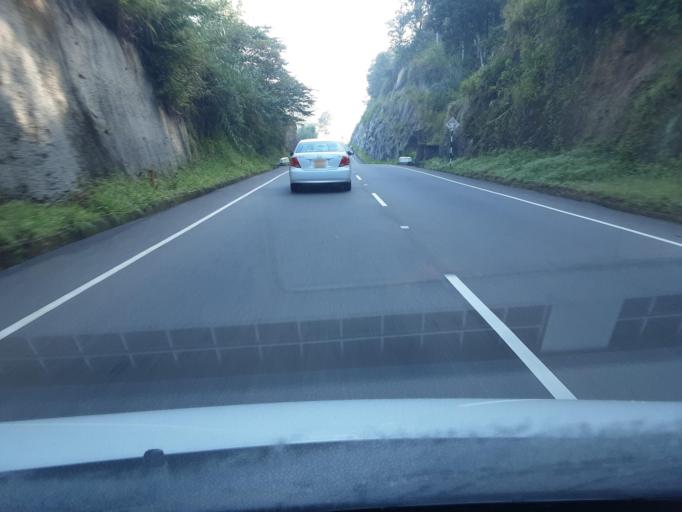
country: LK
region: Uva
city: Badulla
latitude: 6.9123
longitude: 80.9337
